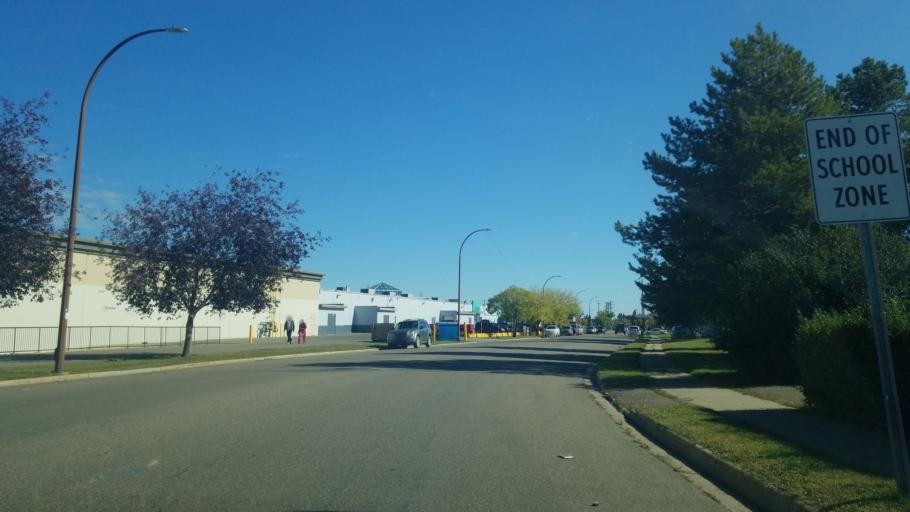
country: CA
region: Saskatchewan
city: Lloydminster
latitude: 53.2761
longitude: -110.0147
